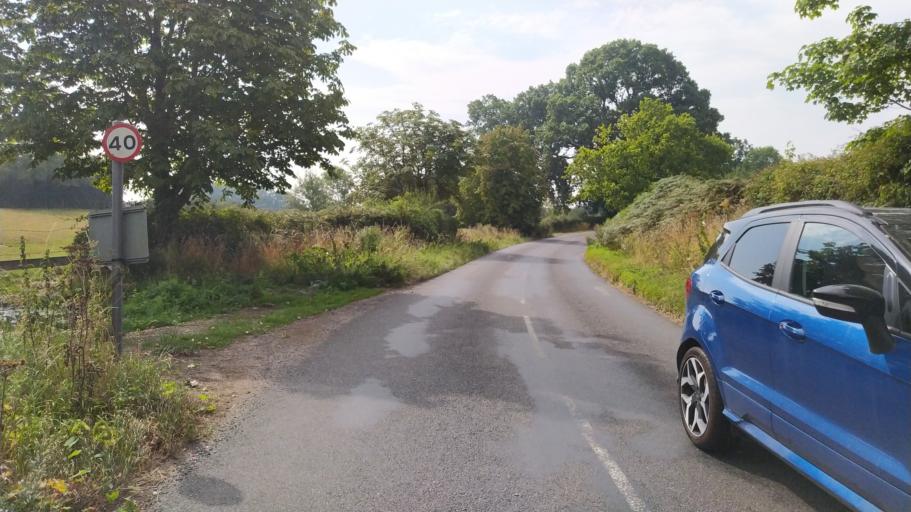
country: GB
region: England
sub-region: Hampshire
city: Chandlers Ford
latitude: 51.0057
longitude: -1.4339
